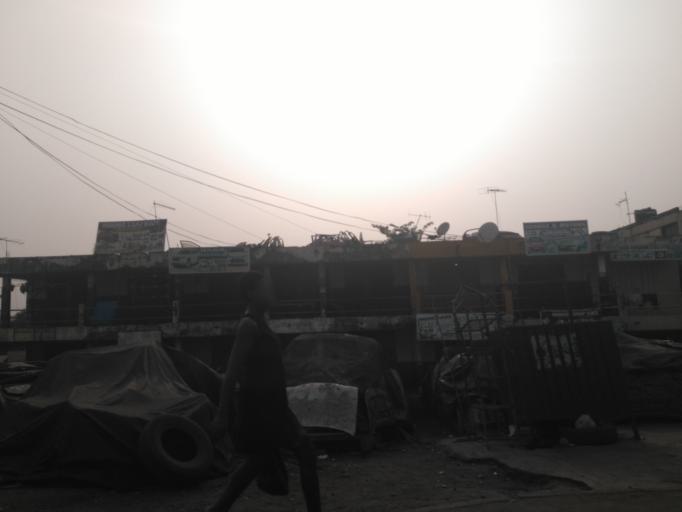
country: GH
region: Ashanti
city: Tafo
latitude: 6.7205
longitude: -1.6326
